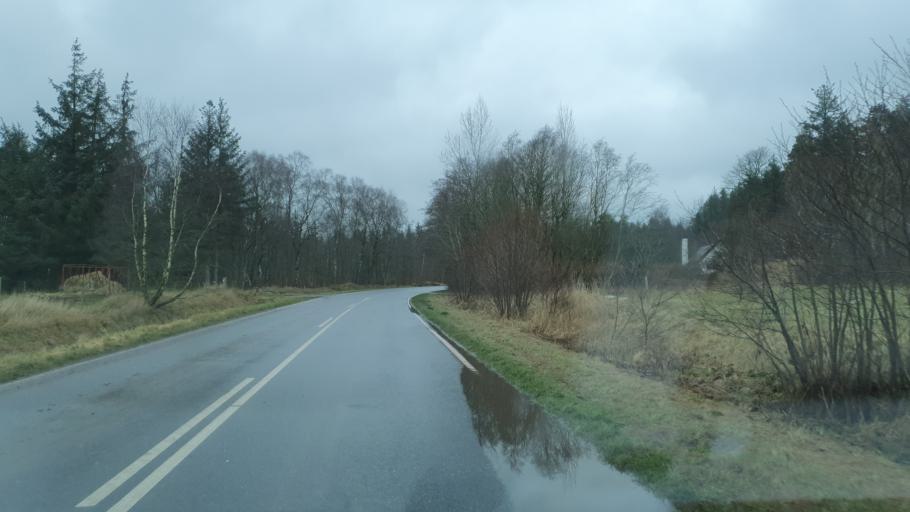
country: DK
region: North Denmark
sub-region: Jammerbugt Kommune
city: Fjerritslev
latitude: 57.1181
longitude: 9.1262
